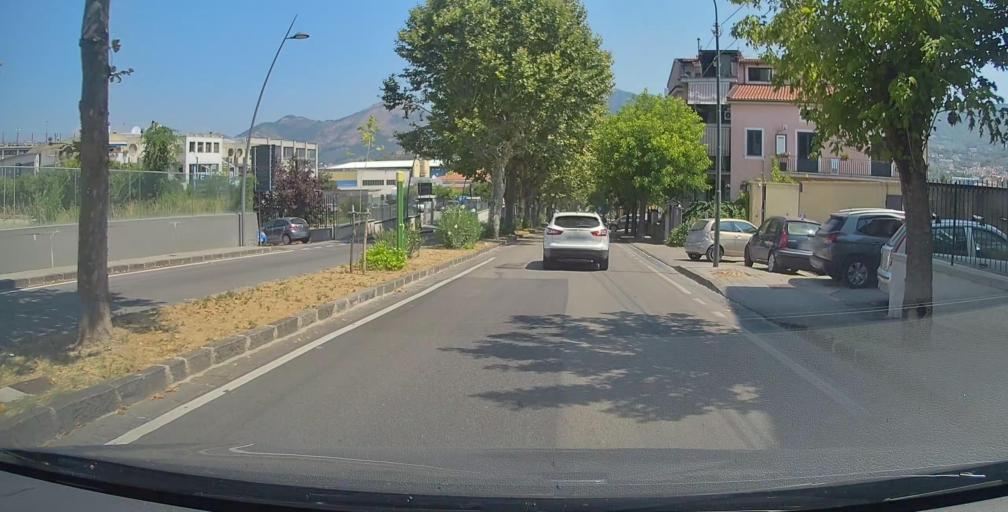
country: IT
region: Campania
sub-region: Provincia di Salerno
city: Cava De Tirreni
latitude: 40.7114
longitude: 14.7006
